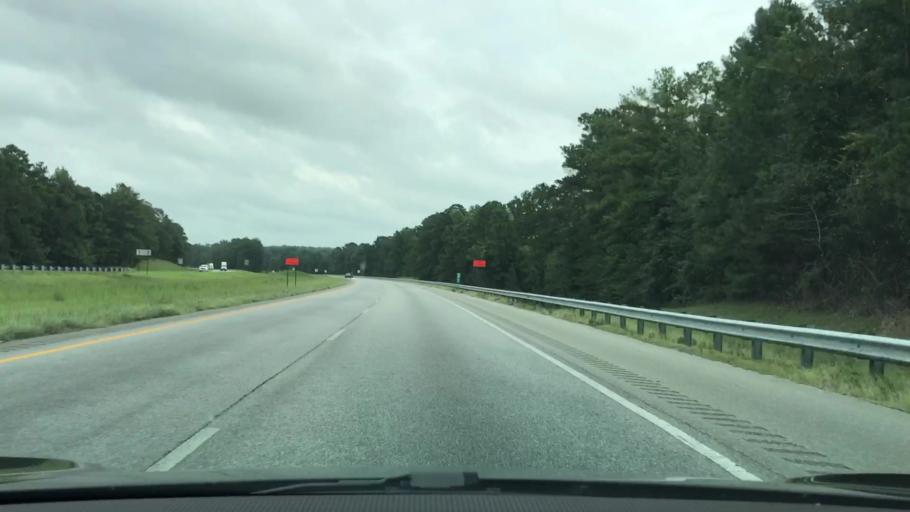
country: US
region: Alabama
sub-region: Lee County
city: Auburn
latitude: 32.5149
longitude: -85.5837
